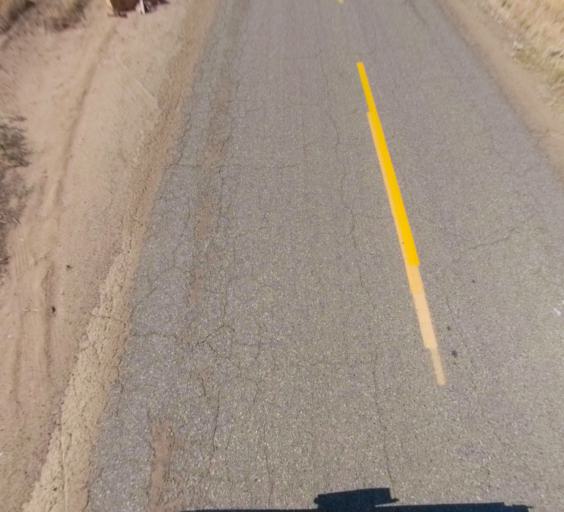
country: US
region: California
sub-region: Madera County
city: Bonadelle Ranchos-Madera Ranchos
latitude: 36.8901
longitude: -119.8109
